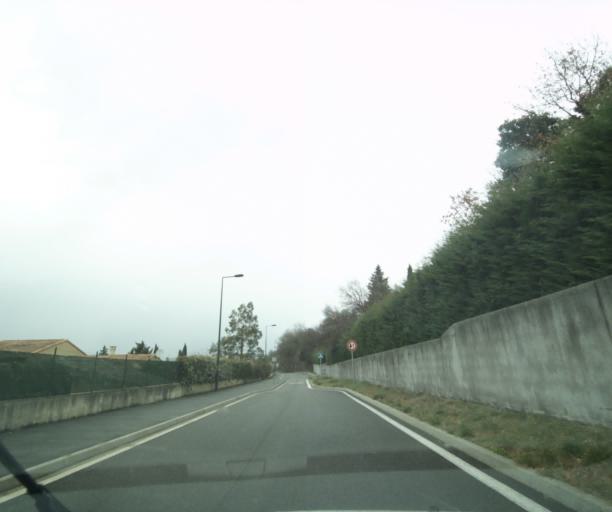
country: FR
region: Rhone-Alpes
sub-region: Departement de la Drome
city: Bourg-les-Valence
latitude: 44.9703
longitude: 4.8996
